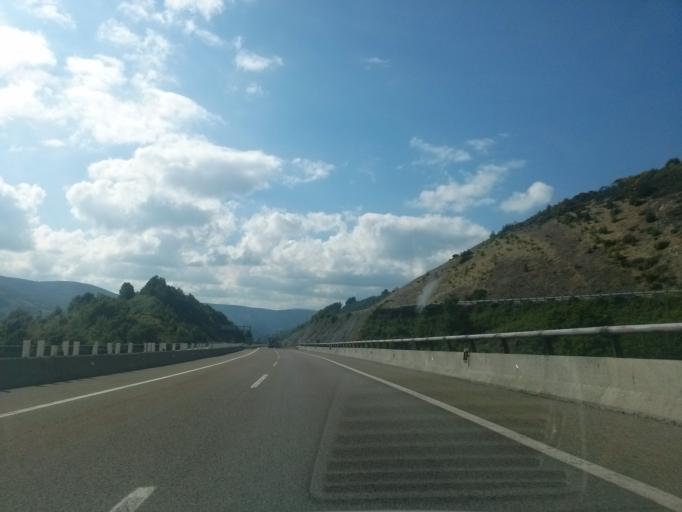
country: ES
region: Galicia
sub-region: Provincia de Lugo
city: San Roman
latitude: 42.7429
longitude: -7.0509
